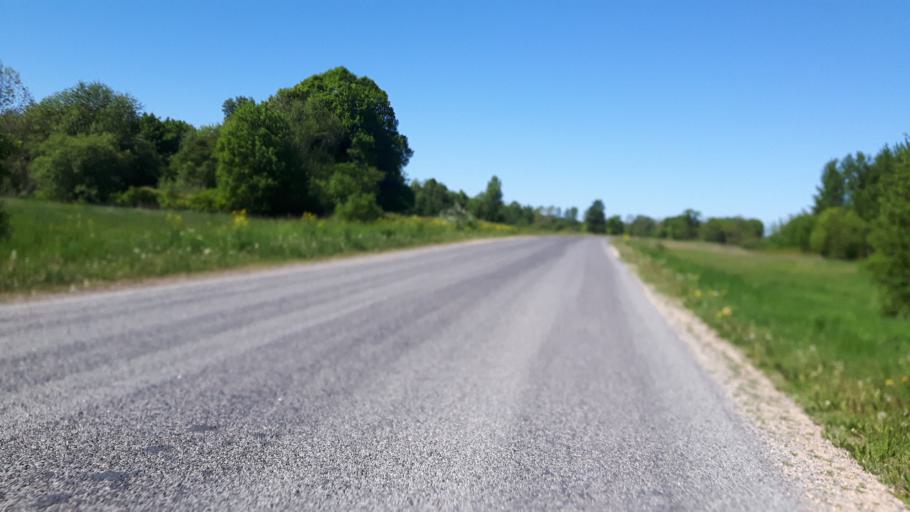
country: EE
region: Ida-Virumaa
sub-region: Sillamaee linn
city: Sillamae
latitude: 59.3780
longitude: 27.8335
